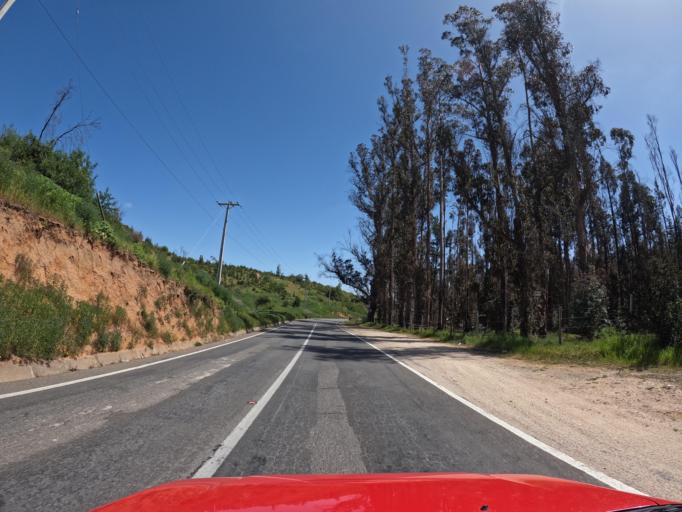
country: CL
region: O'Higgins
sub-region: Provincia de Colchagua
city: Santa Cruz
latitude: -34.6764
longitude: -71.8040
